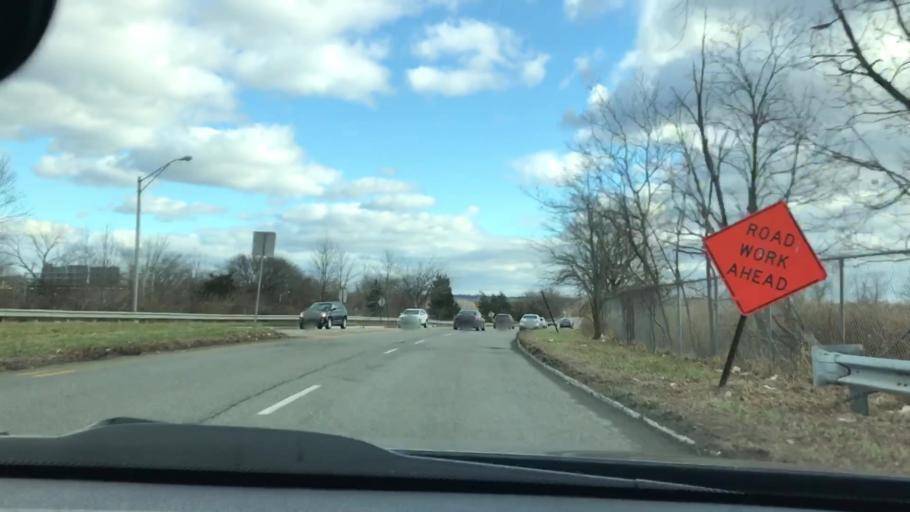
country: US
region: New Jersey
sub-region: Morris County
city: East Hanover
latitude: 40.8464
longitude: -74.3524
